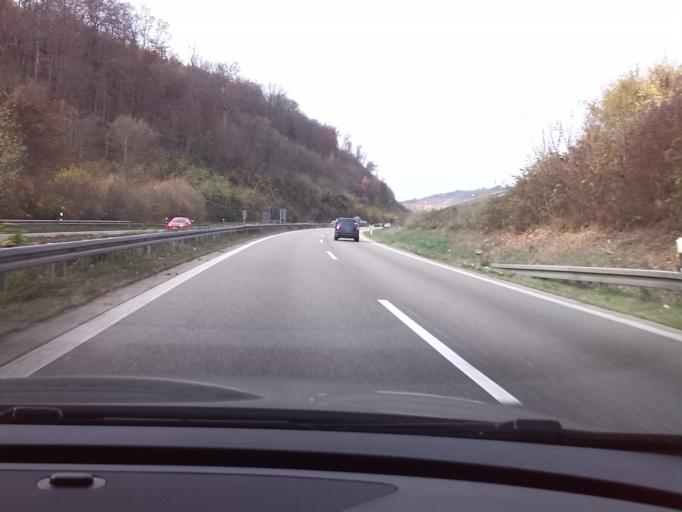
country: DE
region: Baden-Wuerttemberg
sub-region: Regierungsbezirk Stuttgart
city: Esslingen
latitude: 48.7271
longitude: 9.3199
